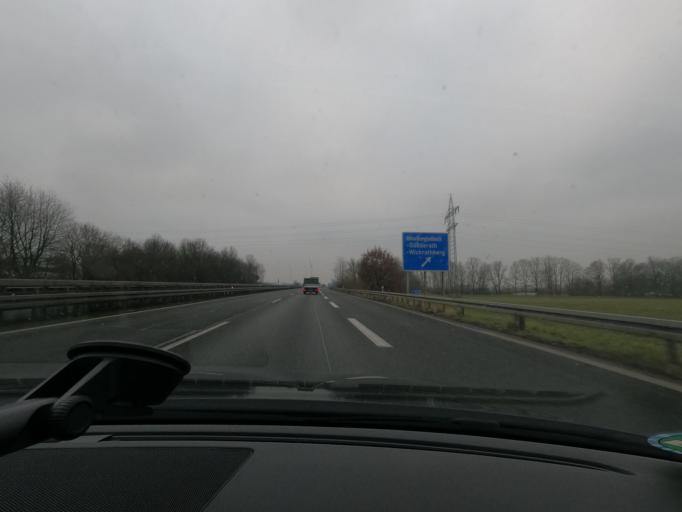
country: DE
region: North Rhine-Westphalia
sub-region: Regierungsbezirk Dusseldorf
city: Monchengladbach
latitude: 51.1199
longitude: 6.4284
